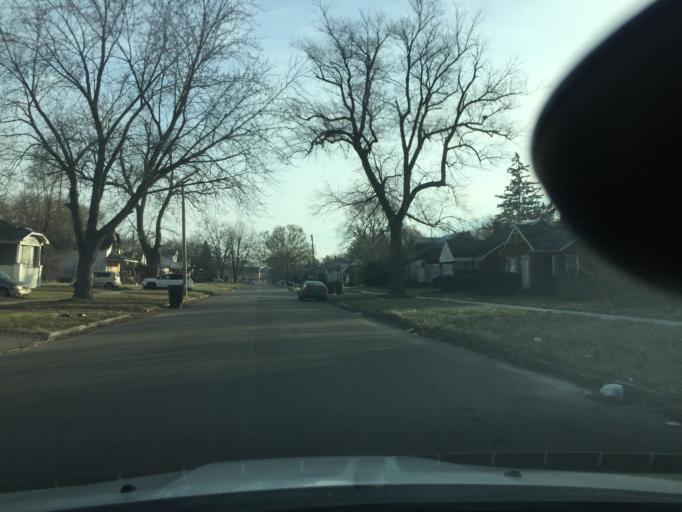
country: US
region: Michigan
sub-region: Macomb County
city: Eastpointe
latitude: 42.4371
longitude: -82.9701
